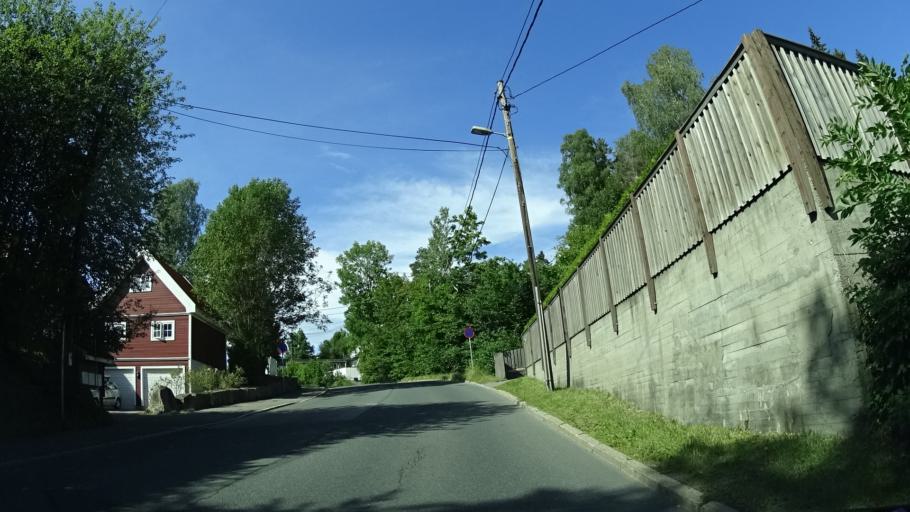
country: NO
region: Oslo
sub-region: Oslo
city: Sjolyststranda
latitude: 59.9547
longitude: 10.6910
